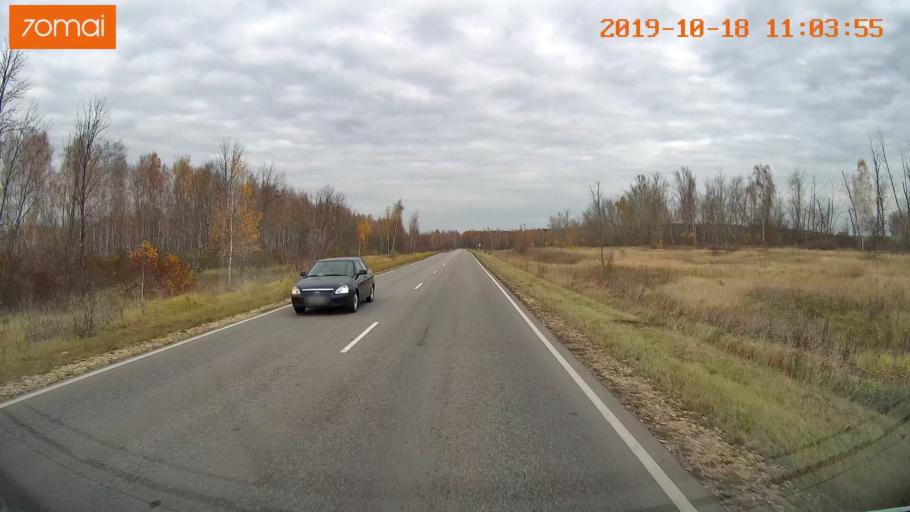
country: RU
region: Tula
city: Yepifan'
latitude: 53.8870
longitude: 38.5498
